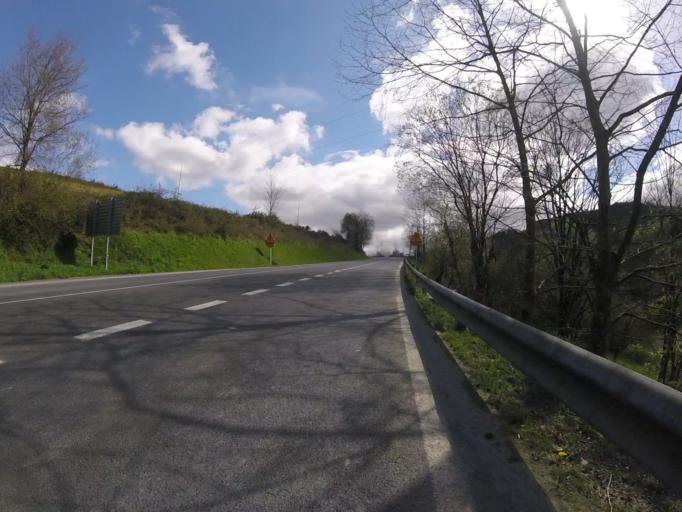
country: ES
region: Basque Country
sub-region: Provincia de Guipuzcoa
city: Astigarraga
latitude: 43.2828
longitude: -1.9262
